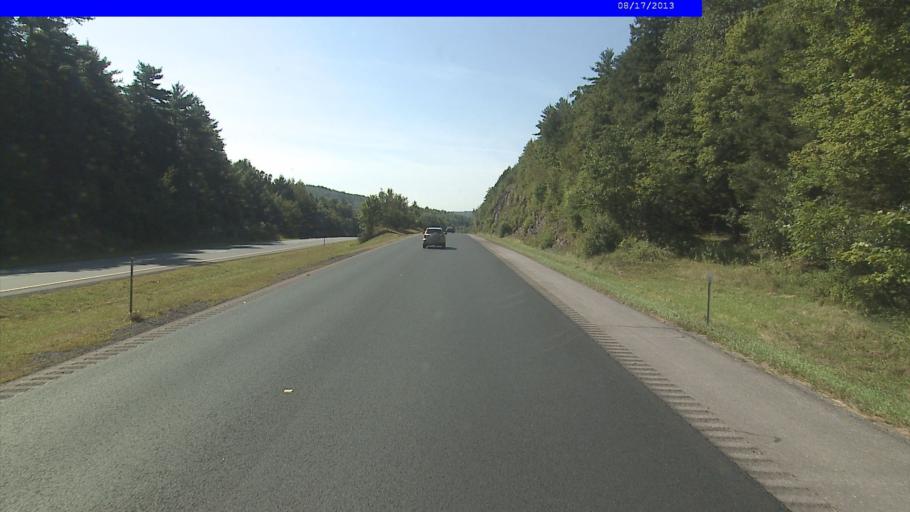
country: US
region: Vermont
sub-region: Windham County
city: Bellows Falls
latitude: 43.1492
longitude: -72.4750
